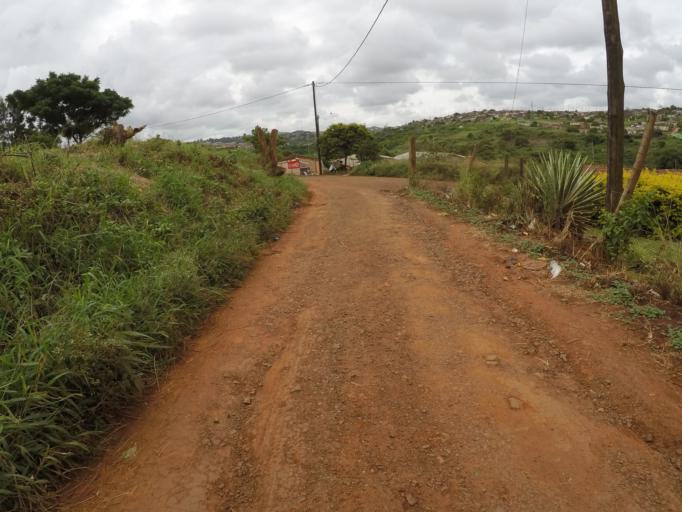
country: ZA
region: KwaZulu-Natal
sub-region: uThungulu District Municipality
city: Empangeni
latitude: -28.7765
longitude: 31.8742
